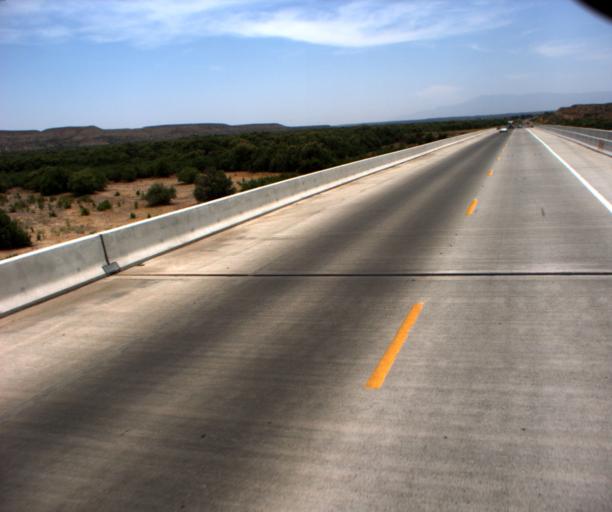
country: US
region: Arizona
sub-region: Graham County
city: Bylas
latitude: 33.1645
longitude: -110.1339
